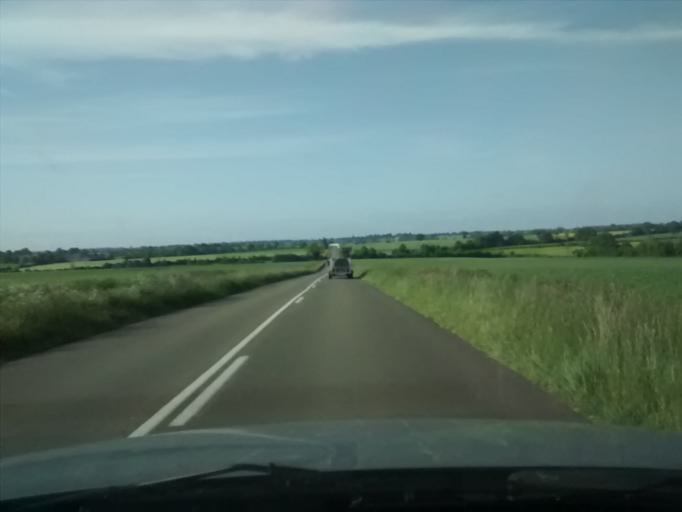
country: FR
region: Pays de la Loire
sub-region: Departement de la Mayenne
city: Soulge-sur-Ouette
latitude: 48.0304
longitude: -0.5772
